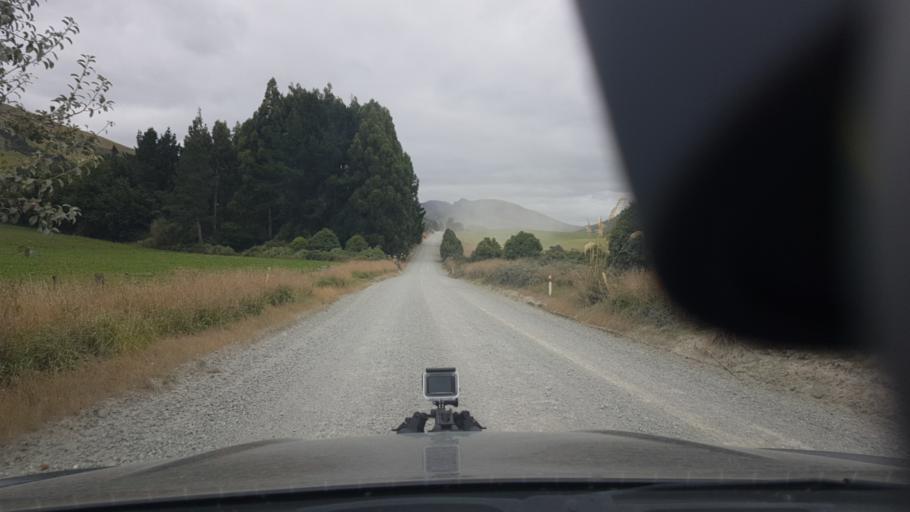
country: NZ
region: Otago
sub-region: Clutha District
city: Papatowai
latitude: -46.3473
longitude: 169.4521
